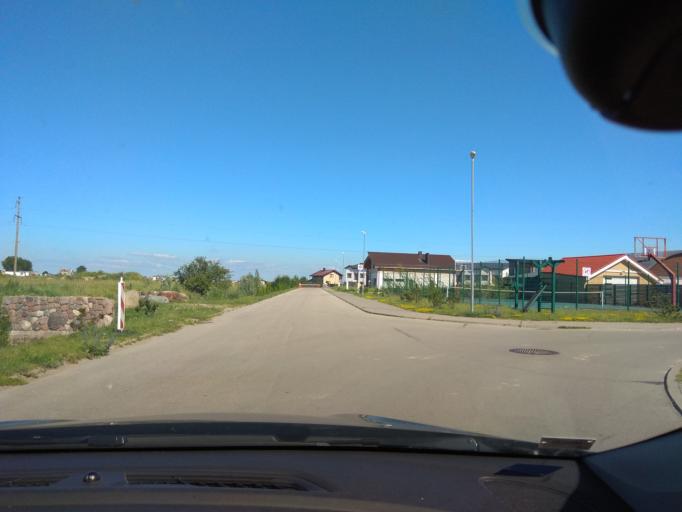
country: LT
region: Klaipedos apskritis
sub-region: Klaipeda
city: Klaipeda
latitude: 55.7491
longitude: 21.1802
